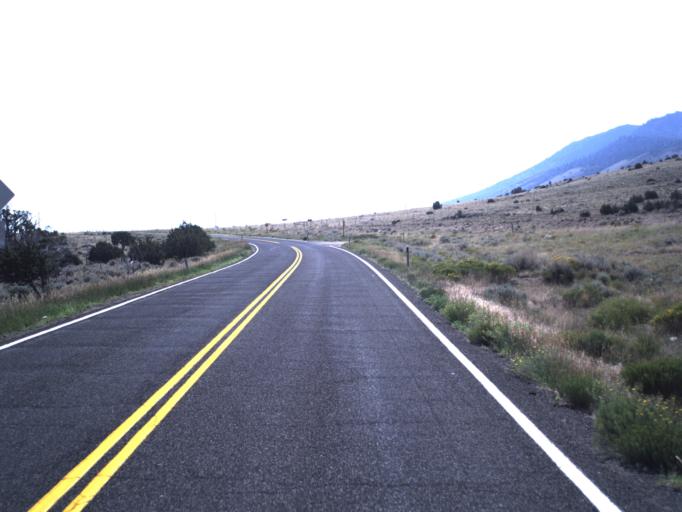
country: US
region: Utah
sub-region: Daggett County
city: Manila
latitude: 40.9769
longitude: -109.8311
